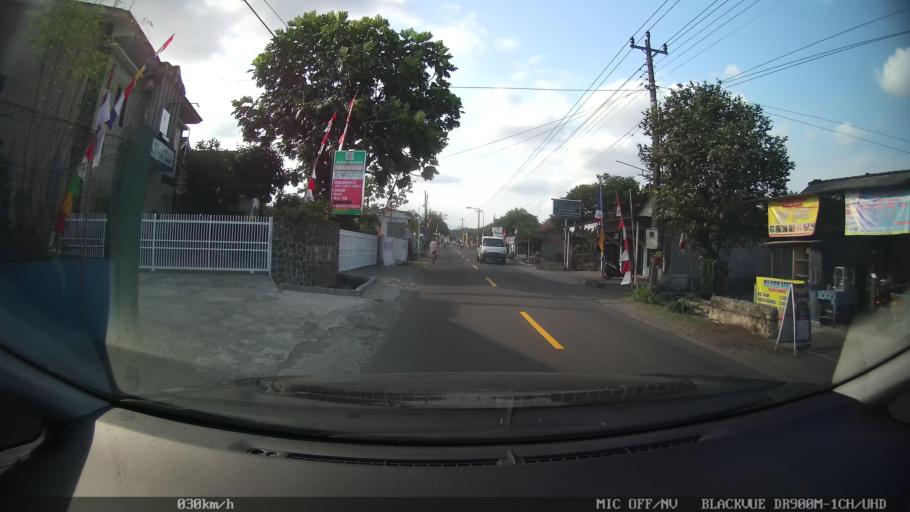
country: ID
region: Central Java
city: Candi Prambanan
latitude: -7.7237
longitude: 110.4724
